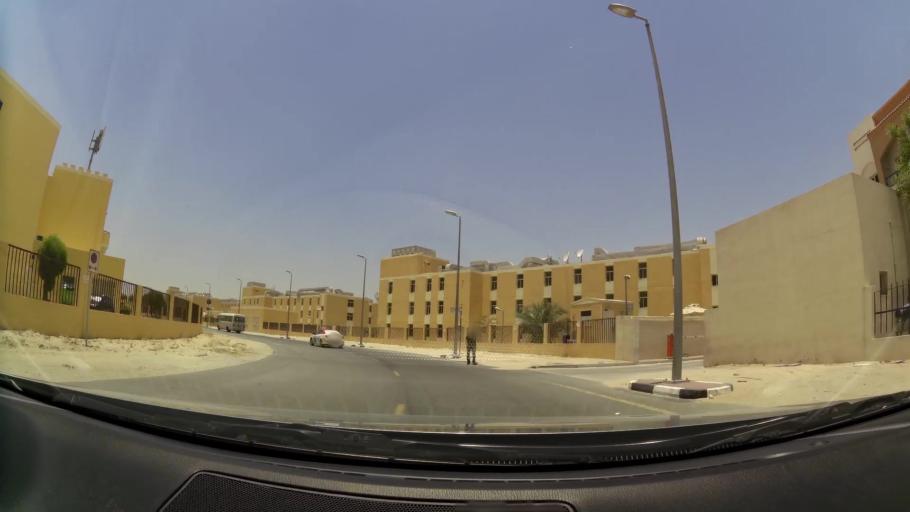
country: AE
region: Dubai
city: Dubai
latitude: 24.9863
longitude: 55.1836
